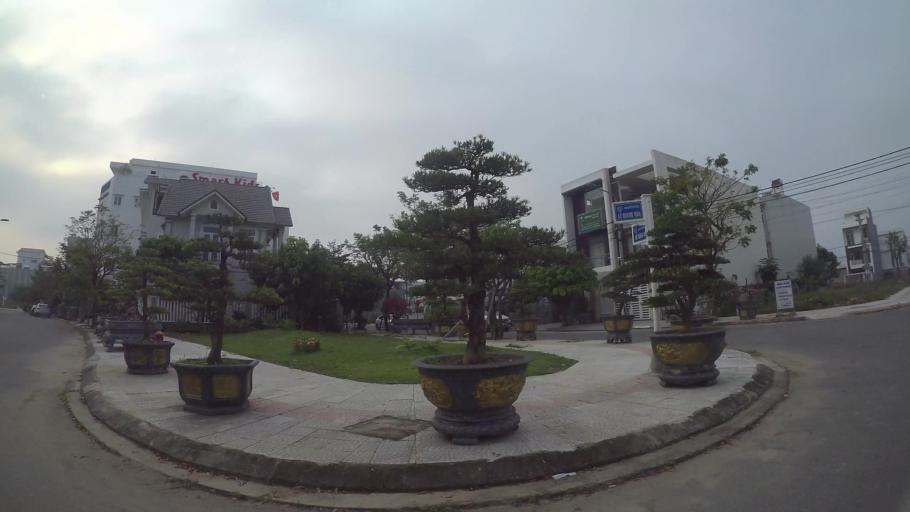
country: VN
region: Da Nang
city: Cam Le
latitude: 16.0228
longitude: 108.2267
